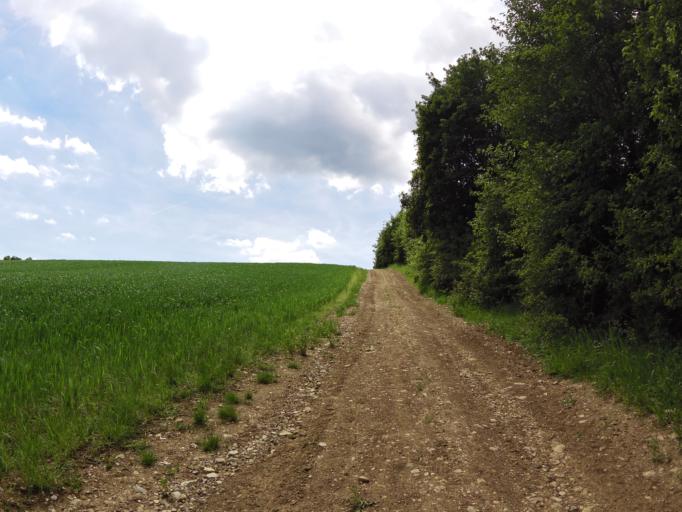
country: DE
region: Bavaria
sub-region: Regierungsbezirk Unterfranken
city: Sommerhausen
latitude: 49.7204
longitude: 10.0345
